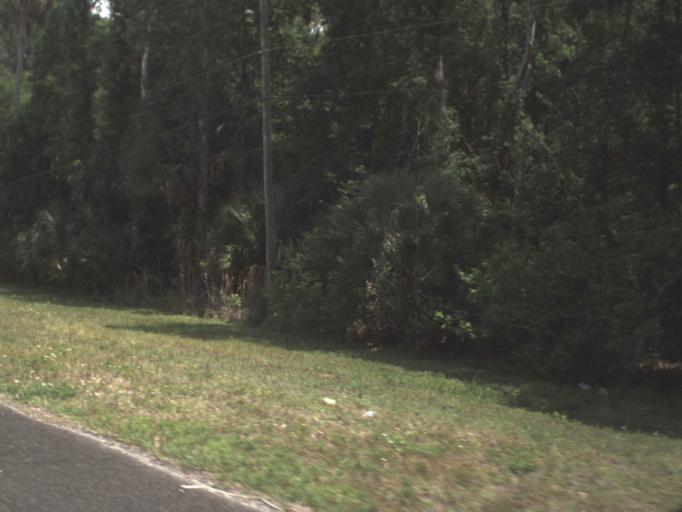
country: US
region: Florida
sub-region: Sumter County
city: Lake Panasoffkee
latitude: 28.8577
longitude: -82.1855
